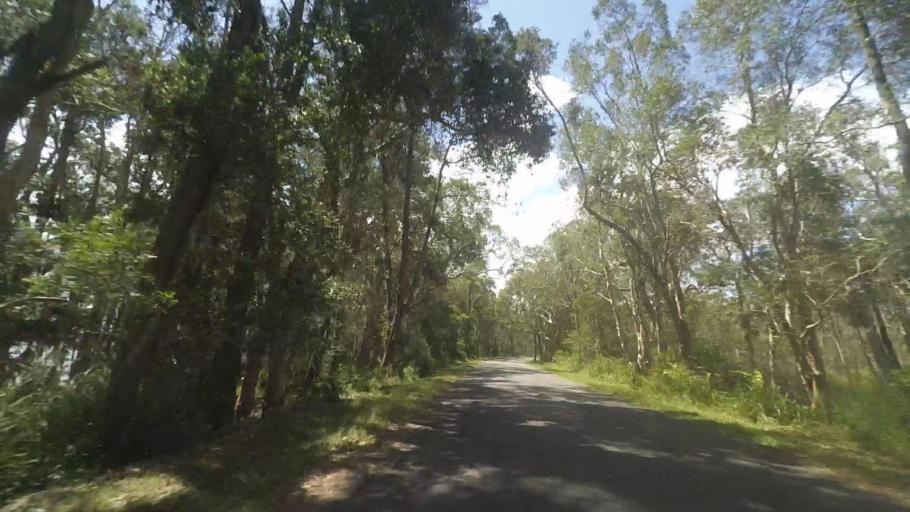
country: AU
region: New South Wales
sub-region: Great Lakes
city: Bulahdelah
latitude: -32.5194
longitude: 152.3223
